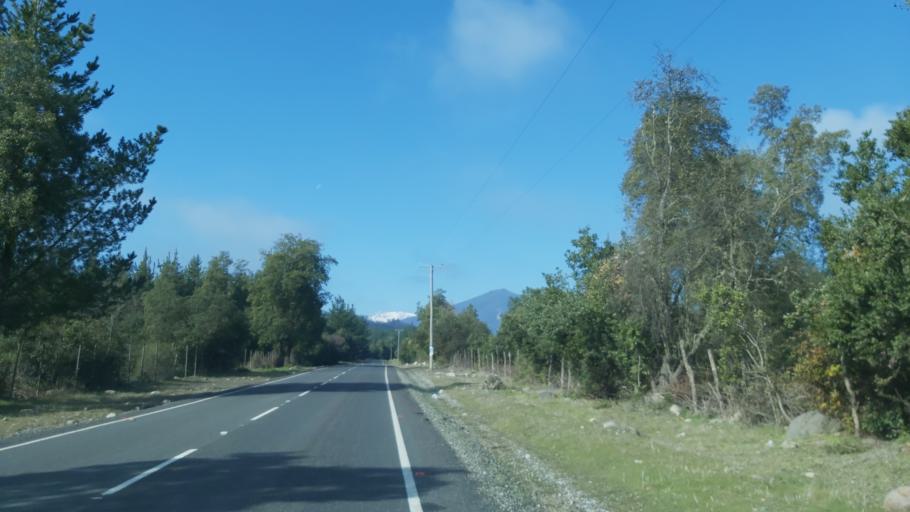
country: CL
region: Maule
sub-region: Provincia de Linares
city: Longavi
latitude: -36.2230
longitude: -71.4711
